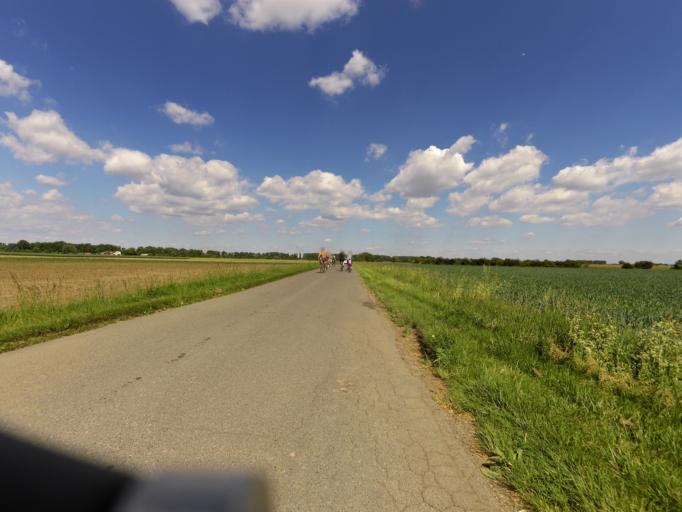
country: DE
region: Rheinland-Pfalz
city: Nackenheim
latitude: 49.9177
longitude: 8.3701
